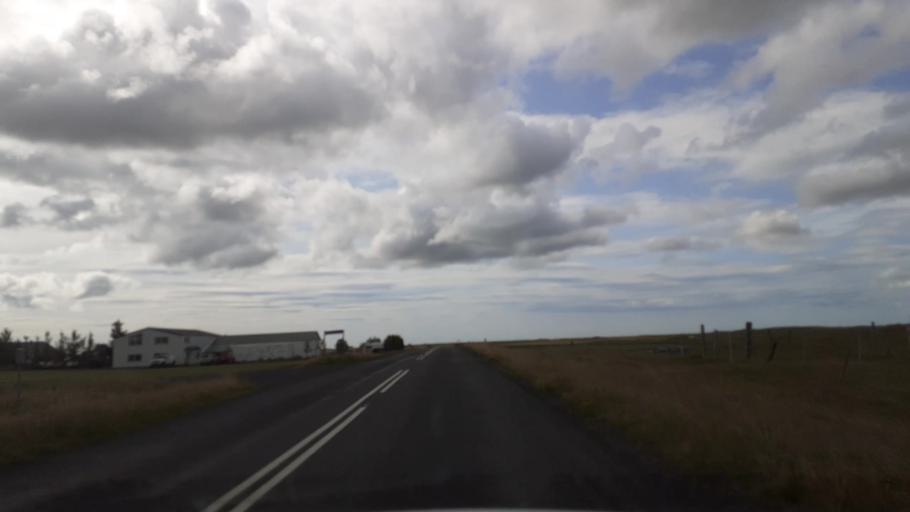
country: IS
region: South
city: Vestmannaeyjar
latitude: 63.8378
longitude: -20.4138
